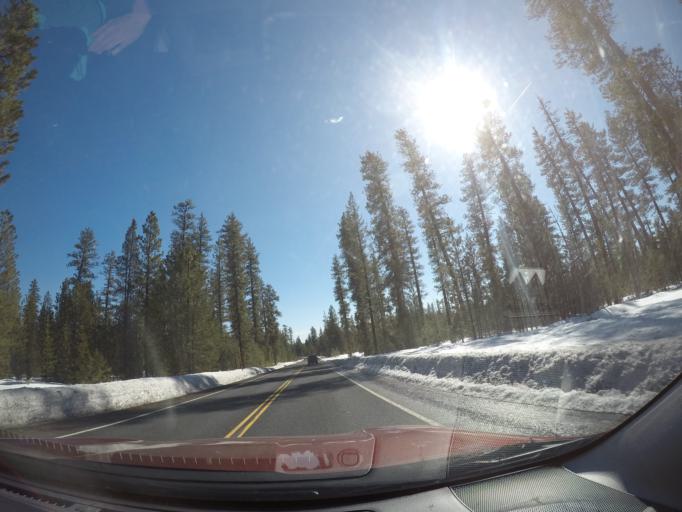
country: US
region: Oregon
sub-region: Deschutes County
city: Three Rivers
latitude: 43.8949
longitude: -121.5903
